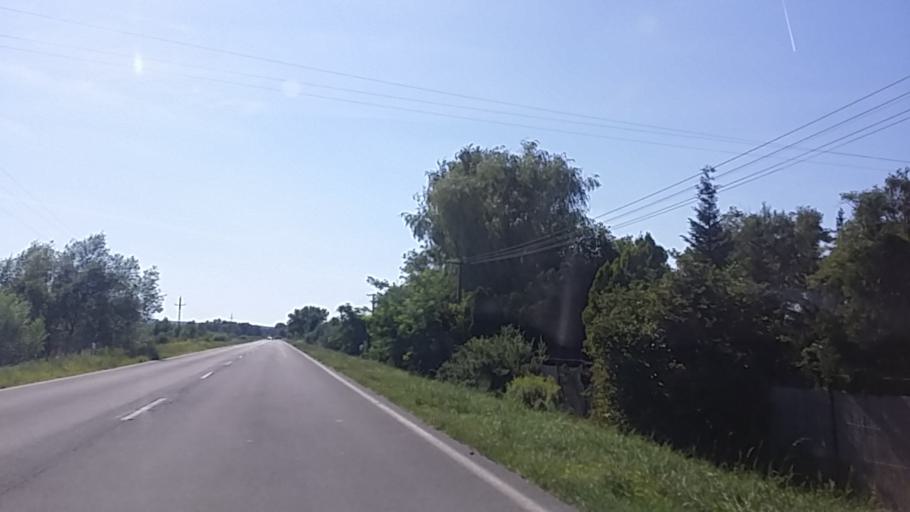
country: HU
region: Somogy
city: Kethely
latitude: 46.6986
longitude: 17.4236
